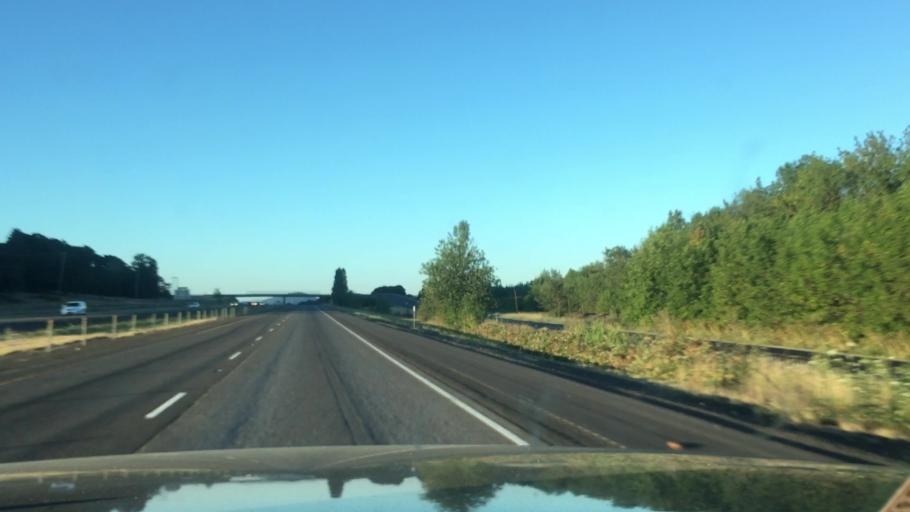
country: US
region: Oregon
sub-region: Lane County
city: Creswell
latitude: 43.9749
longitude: -123.0106
